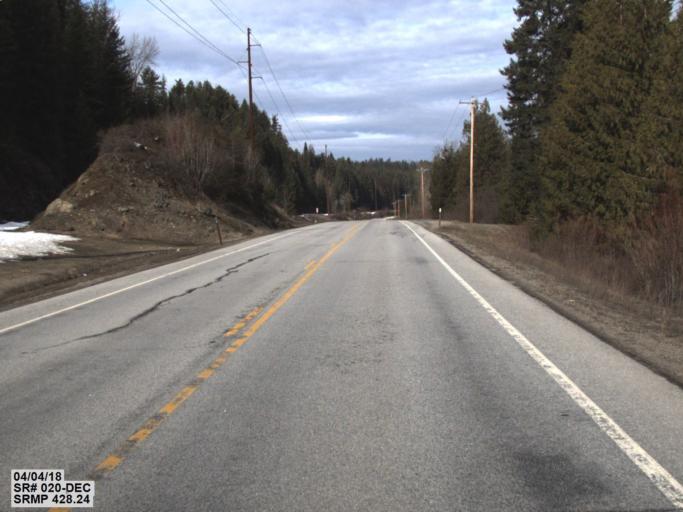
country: US
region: Washington
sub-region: Pend Oreille County
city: Newport
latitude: 48.2311
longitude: -117.1998
